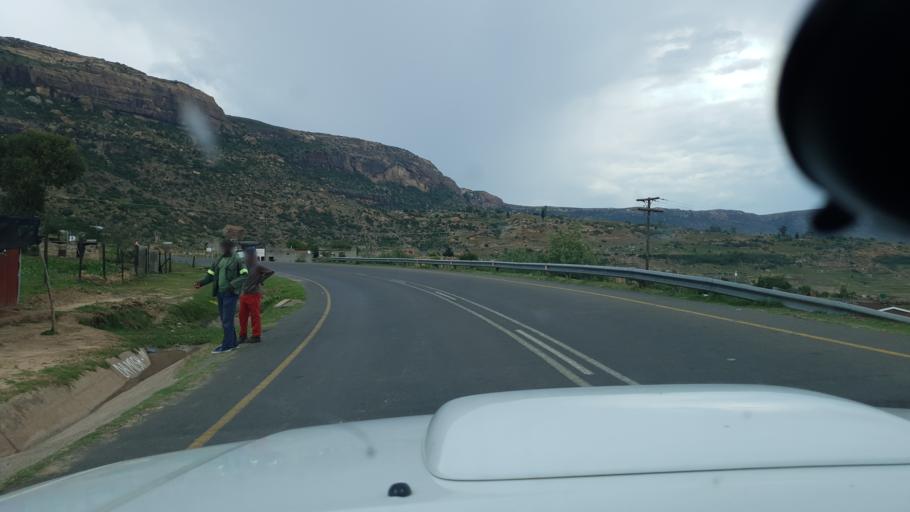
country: LS
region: Maseru
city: Maseru
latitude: -29.4651
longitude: 27.5006
